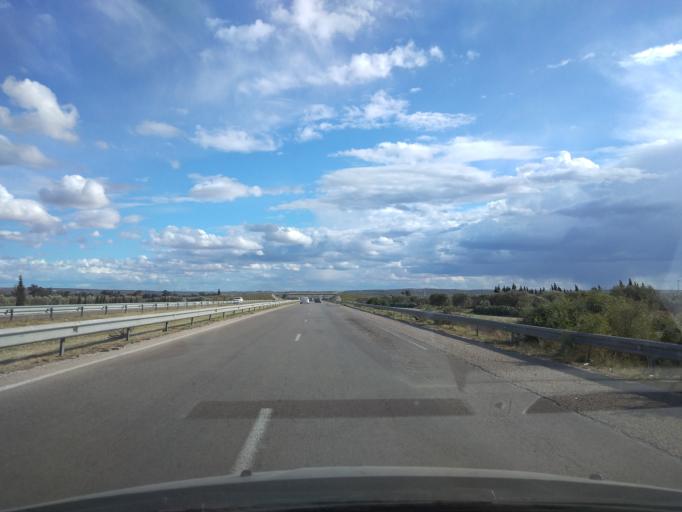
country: TN
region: Al Munastir
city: Manzil Kamil
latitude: 35.5956
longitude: 10.6027
